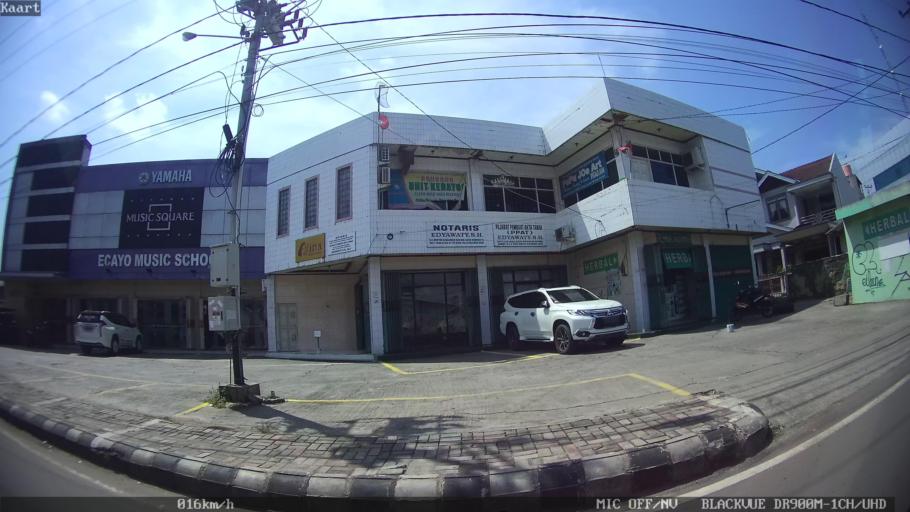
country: ID
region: Lampung
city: Kedaton
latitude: -5.3790
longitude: 105.2601
